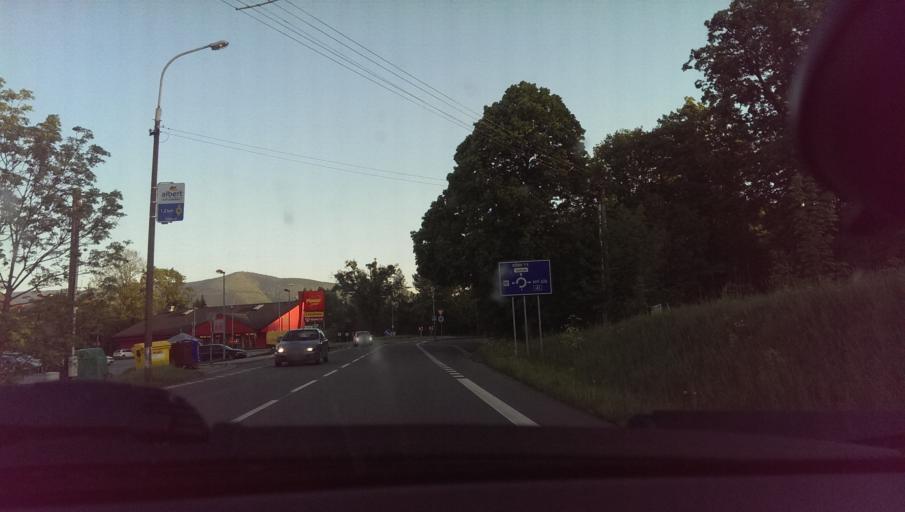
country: CZ
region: Moravskoslezsky
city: Frenstat pod Radhostem
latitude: 49.5521
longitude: 18.1997
